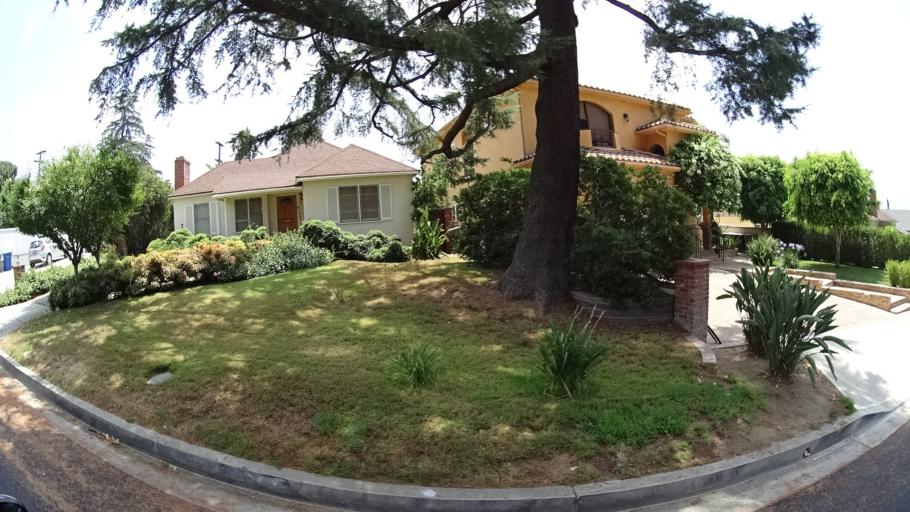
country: US
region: California
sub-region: Los Angeles County
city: Burbank
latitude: 34.1876
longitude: -118.2902
